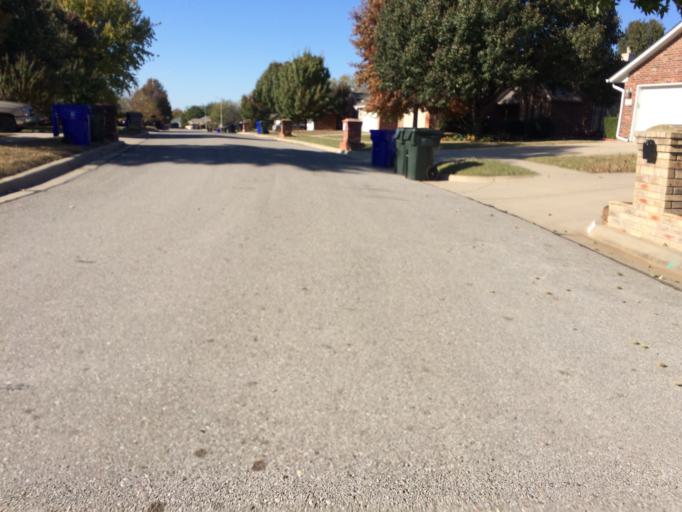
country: US
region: Oklahoma
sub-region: Cleveland County
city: Noble
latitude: 35.1701
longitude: -97.4271
